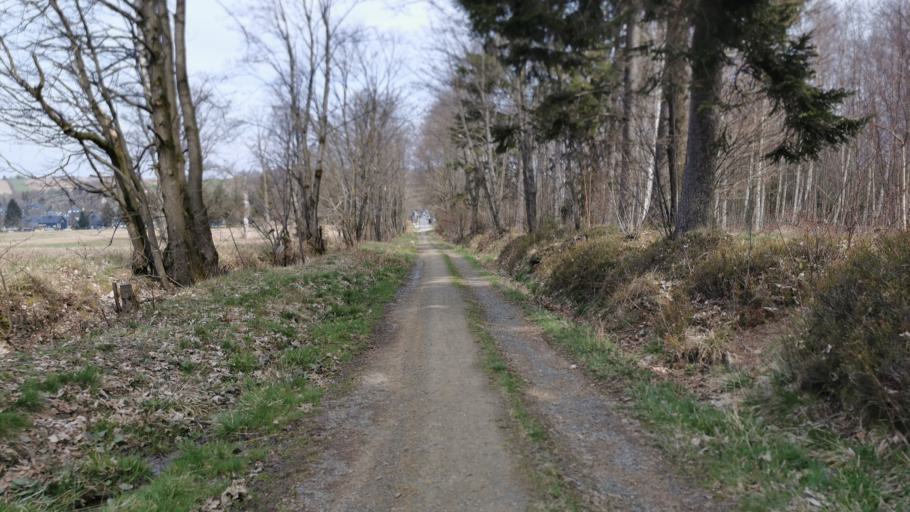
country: DE
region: Bavaria
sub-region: Upper Franconia
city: Reichenbach
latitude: 50.4697
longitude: 11.4545
